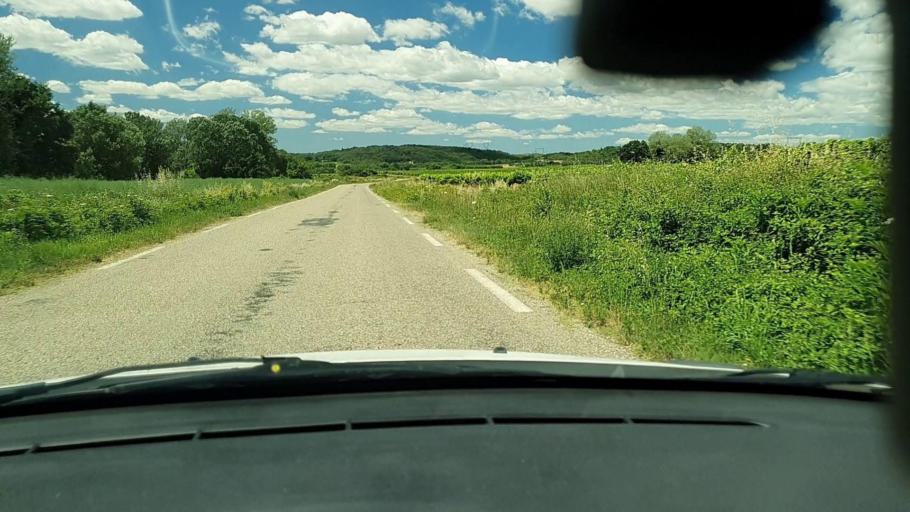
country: FR
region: Languedoc-Roussillon
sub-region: Departement du Gard
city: Blauzac
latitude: 43.9524
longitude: 4.4022
